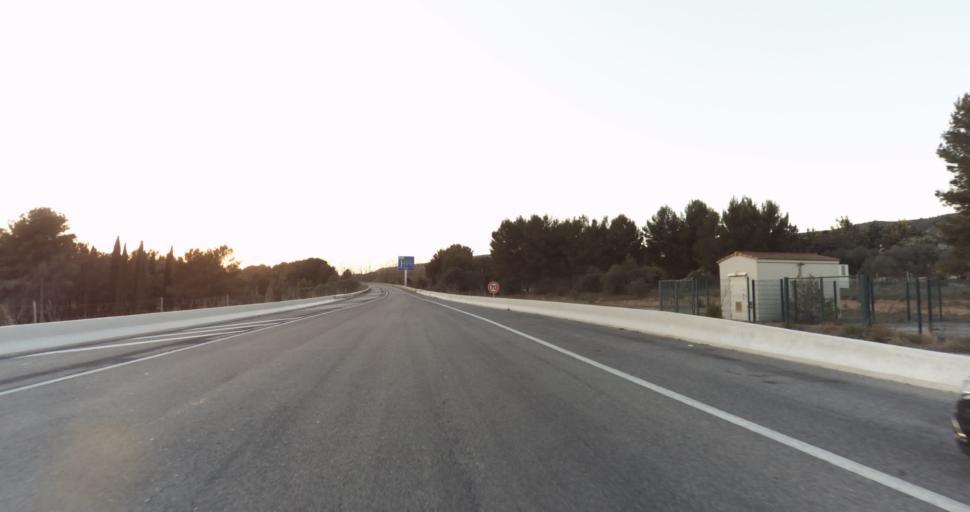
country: FR
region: Provence-Alpes-Cote d'Azur
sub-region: Departement des Bouches-du-Rhone
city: Coudoux
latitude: 43.5532
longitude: 5.2381
